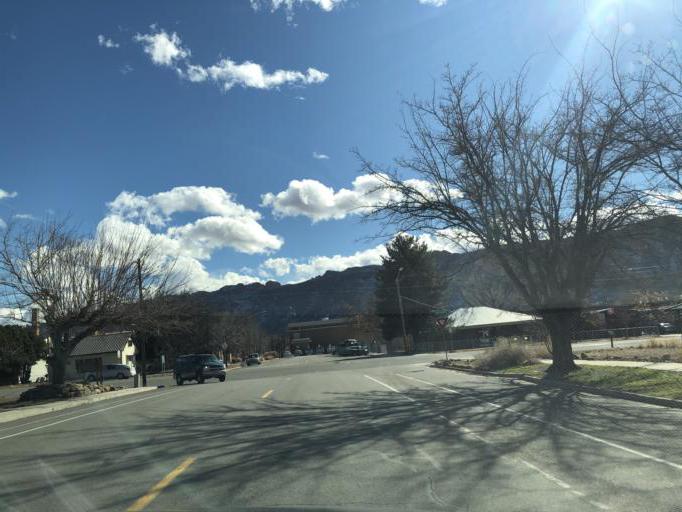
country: US
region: Utah
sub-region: Grand County
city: Moab
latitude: 38.5754
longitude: -109.5469
